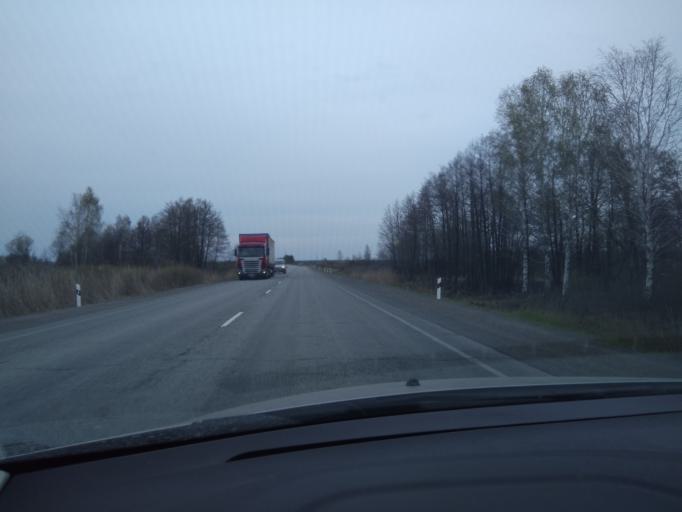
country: RU
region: Sverdlovsk
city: Pyshma
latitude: 57.0228
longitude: 63.3976
